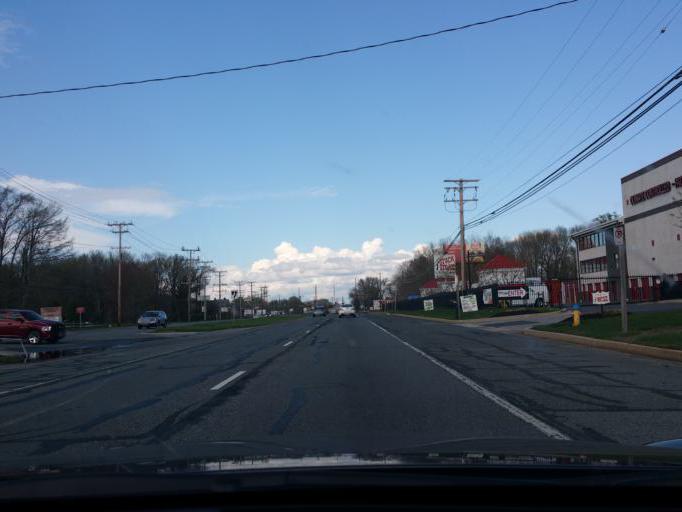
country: US
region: Maryland
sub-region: Harford County
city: Havre de Grace
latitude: 39.5329
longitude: -76.1205
